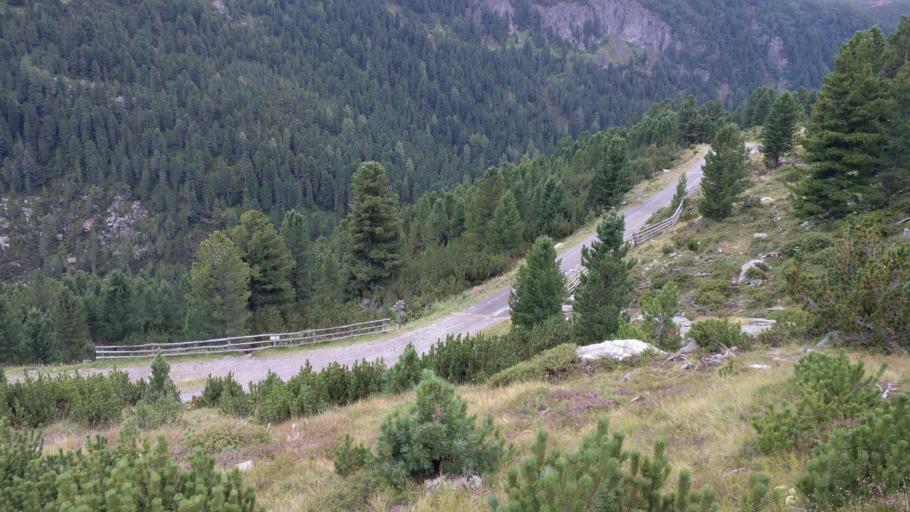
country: IT
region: Trentino-Alto Adige
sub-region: Bolzano
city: Villandro - Villanders
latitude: 46.6928
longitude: 11.4731
